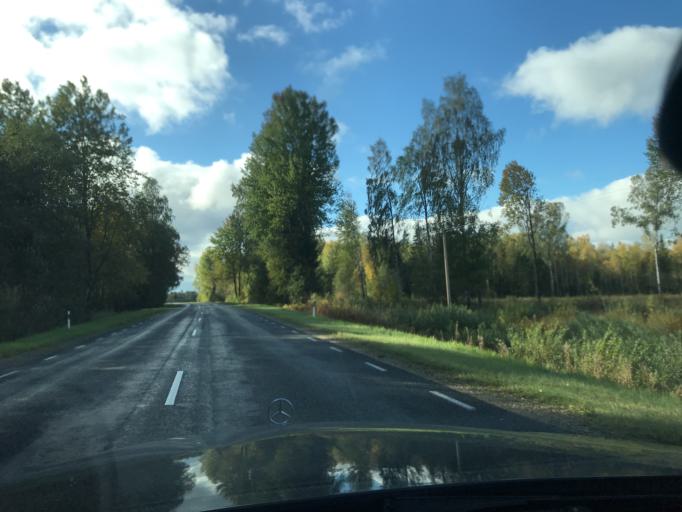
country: EE
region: Tartu
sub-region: Elva linn
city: Elva
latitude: 57.9931
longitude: 26.2646
